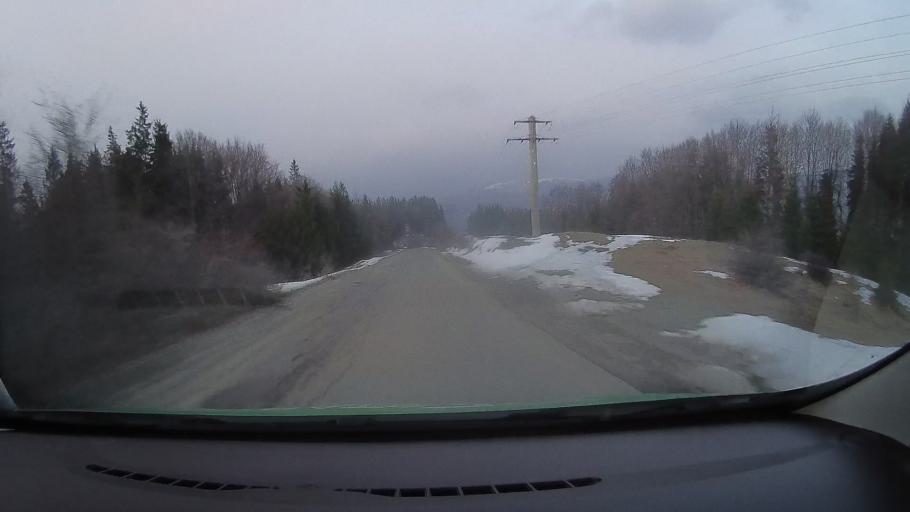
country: RO
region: Prahova
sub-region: Comuna Secaria
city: Secaria
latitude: 45.2884
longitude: 25.7022
